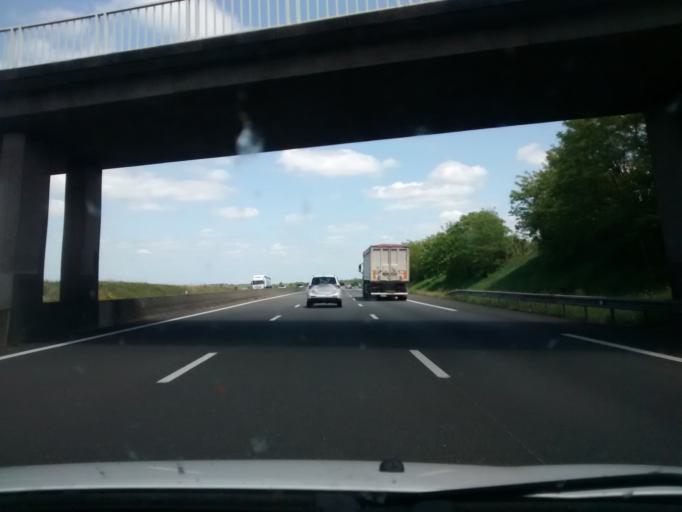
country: FR
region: Centre
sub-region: Departement d'Eure-et-Loir
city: Brou
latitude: 48.2693
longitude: 1.1573
